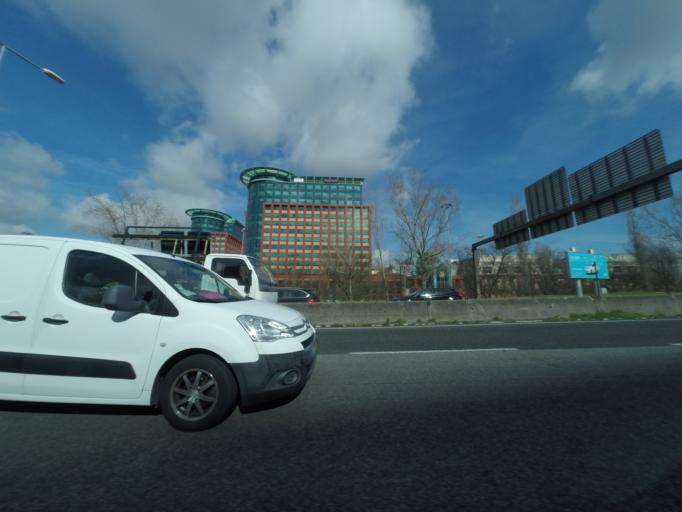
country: PT
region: Lisbon
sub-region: Odivelas
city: Pontinha
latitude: 38.7533
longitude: -9.1860
